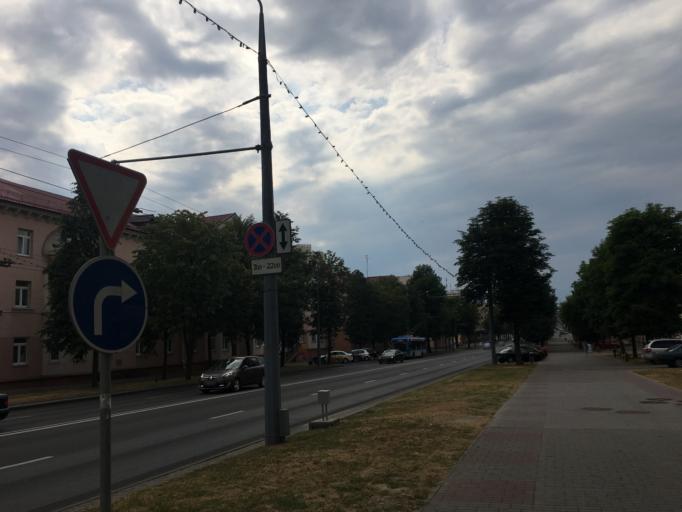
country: BY
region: Grodnenskaya
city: Hrodna
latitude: 53.6757
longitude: 23.8497
